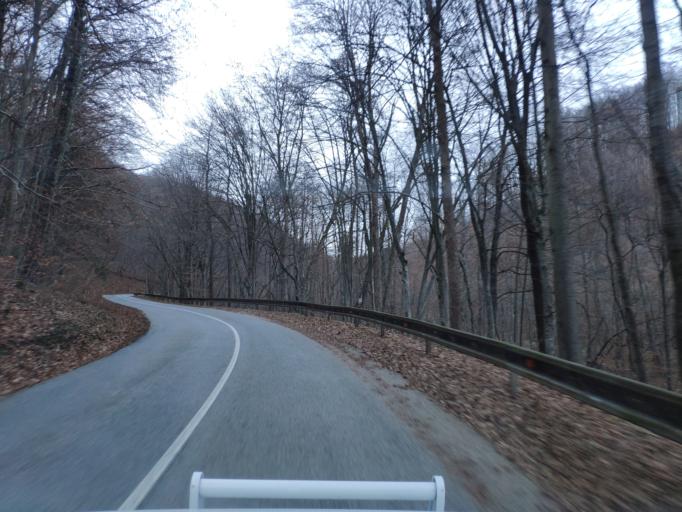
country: SK
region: Kosicky
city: Dobsina
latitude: 48.7776
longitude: 20.4759
